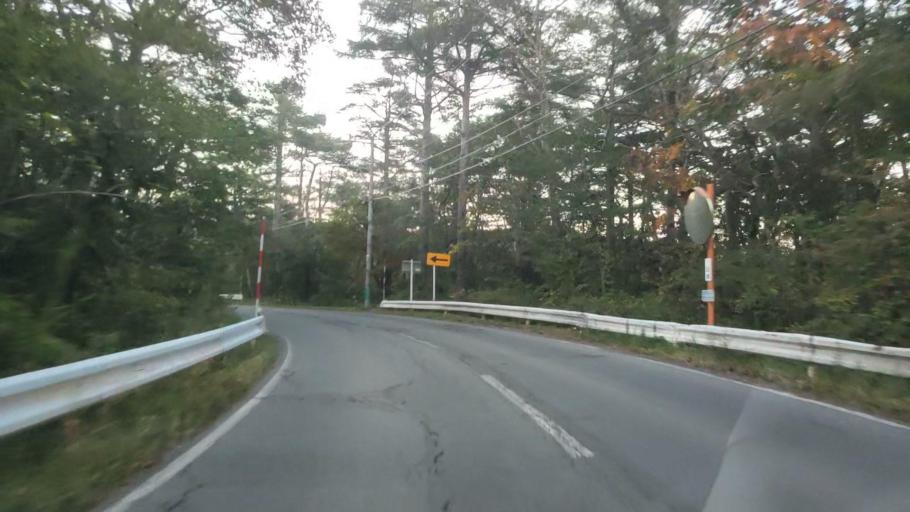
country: JP
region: Nagano
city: Komoro
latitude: 36.3980
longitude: 138.5813
